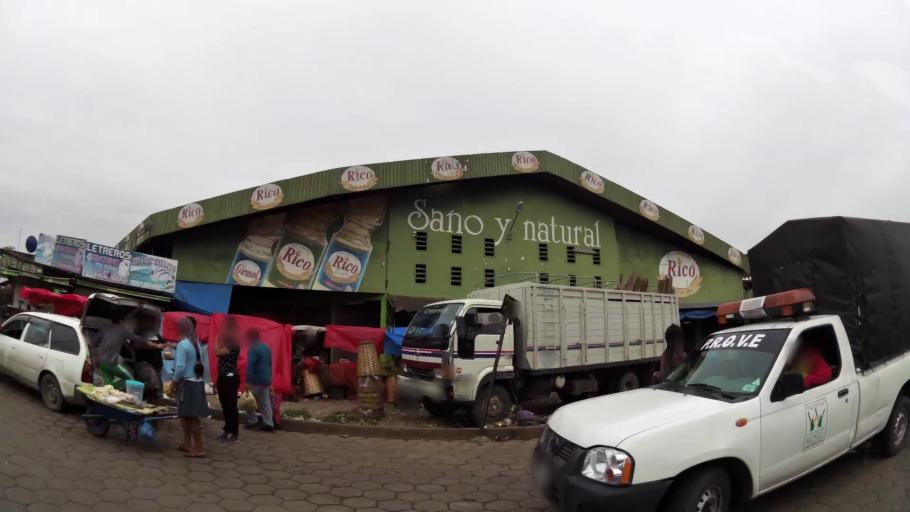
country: BO
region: Santa Cruz
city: Santa Cruz de la Sierra
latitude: -17.7950
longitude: -63.2052
